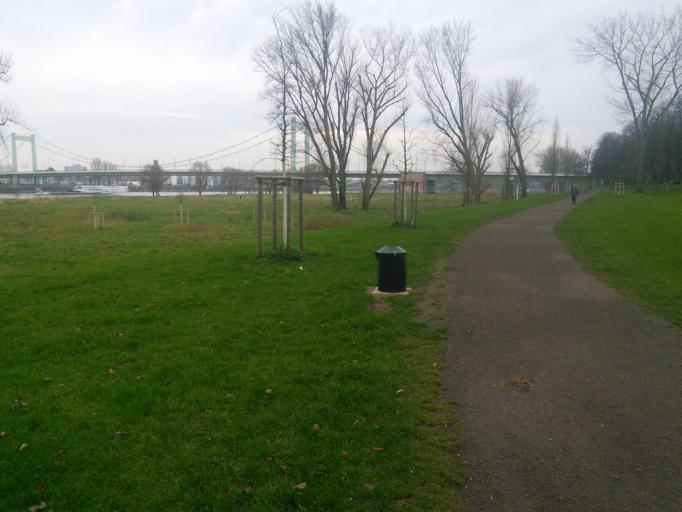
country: DE
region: North Rhine-Westphalia
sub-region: Regierungsbezirk Koln
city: Muelheim
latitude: 50.9682
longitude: 6.9926
